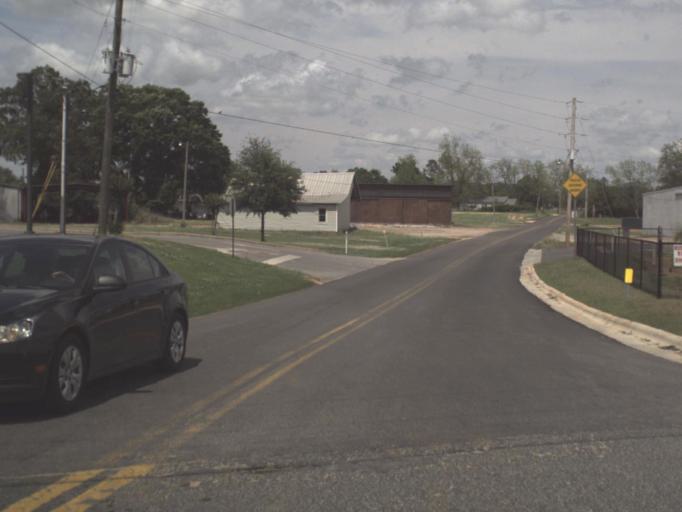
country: US
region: Florida
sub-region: Escambia County
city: Century
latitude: 30.9530
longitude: -87.1504
